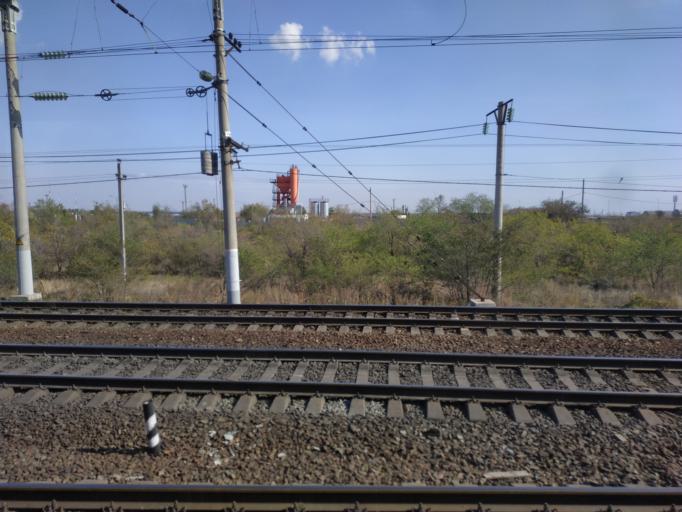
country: RU
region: Volgograd
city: Gumrak
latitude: 48.7917
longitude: 44.3664
